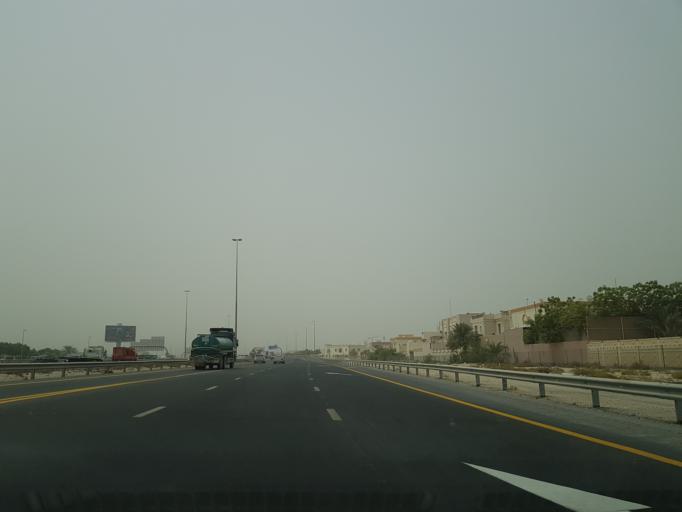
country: AE
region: Dubai
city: Dubai
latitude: 25.1660
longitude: 55.2661
